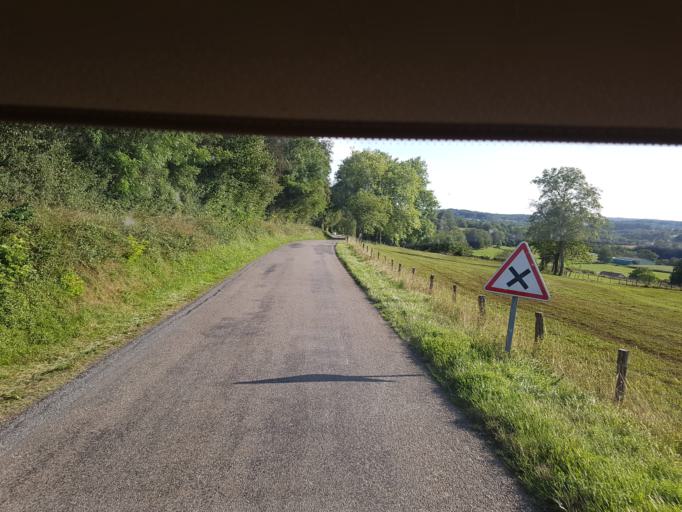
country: FR
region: Rhone-Alpes
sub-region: Departement de l'Ain
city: Poncin
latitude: 46.1158
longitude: 5.3996
